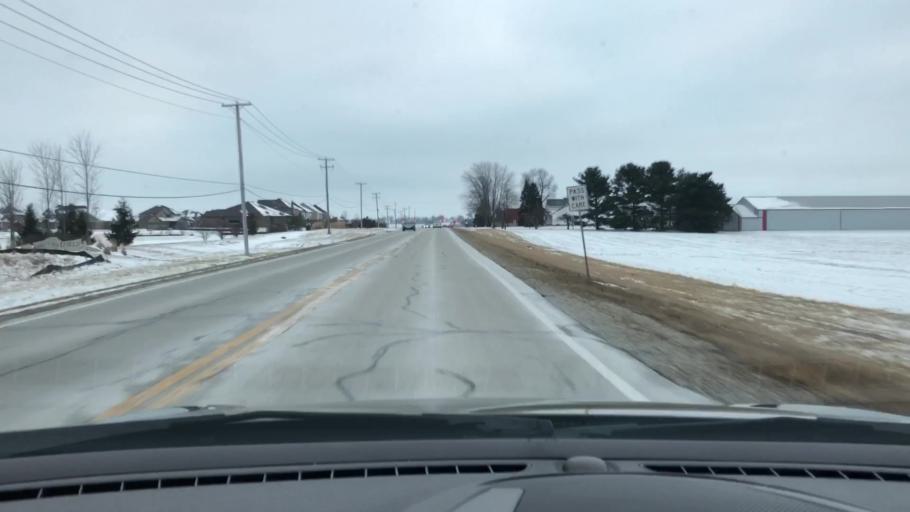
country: US
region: Illinois
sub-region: Will County
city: New Lenox
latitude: 41.4877
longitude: -88.0034
